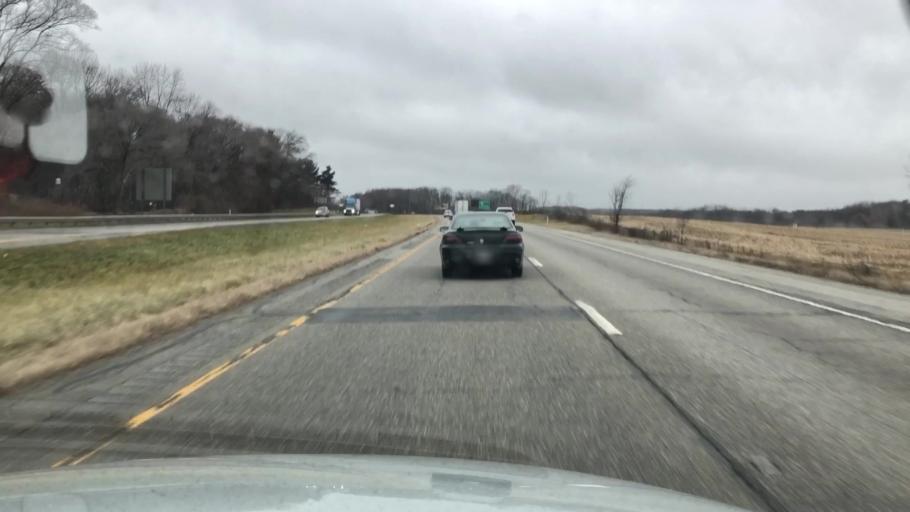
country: US
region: Indiana
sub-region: Marshall County
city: Plymouth
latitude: 41.3613
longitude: -86.2943
